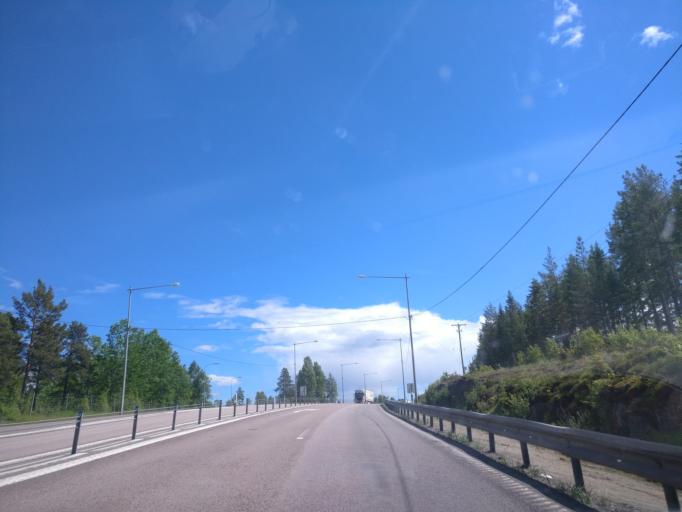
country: SE
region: Vaesternorrland
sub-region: Haernoesands Kommun
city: Haernoesand
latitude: 62.6549
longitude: 17.8797
